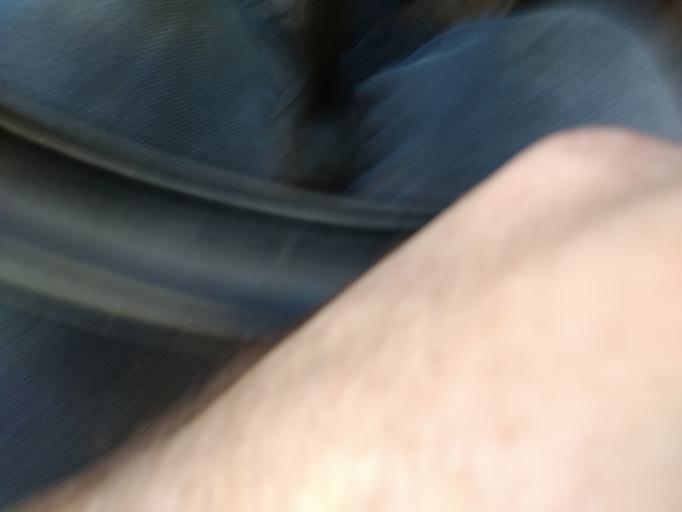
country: BZ
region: Cayo
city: San Ignacio
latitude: 17.2567
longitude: -88.9957
